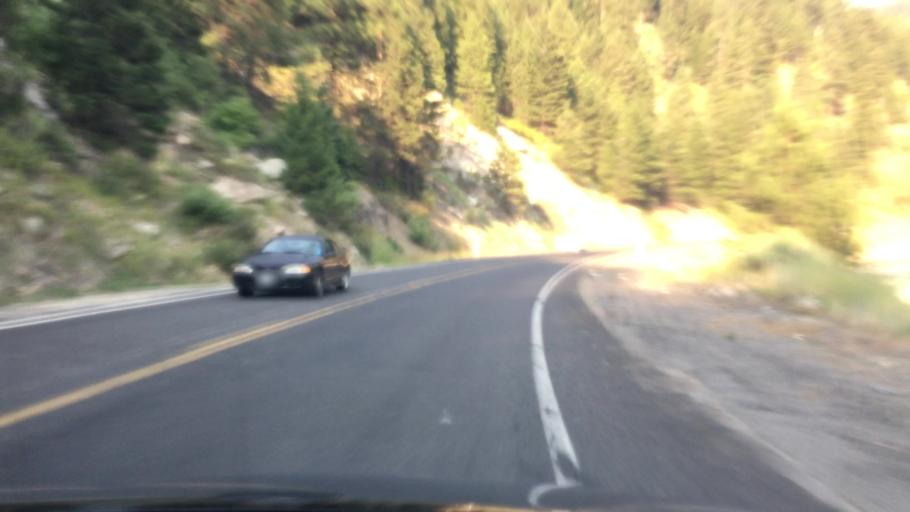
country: US
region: Idaho
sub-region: Valley County
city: Cascade
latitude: 44.2633
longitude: -116.0761
